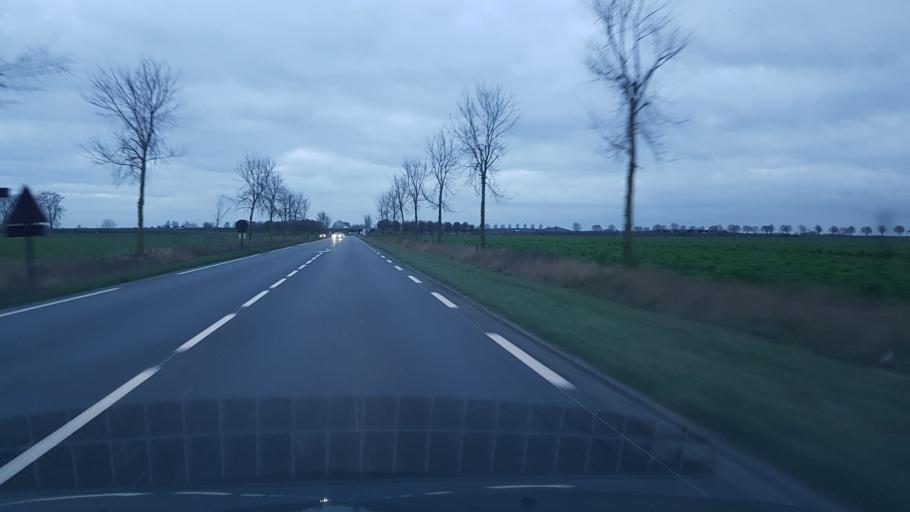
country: FR
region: Ile-de-France
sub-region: Departement de Seine-et-Marne
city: Moissy-Cramayel
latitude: 48.6310
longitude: 2.6370
